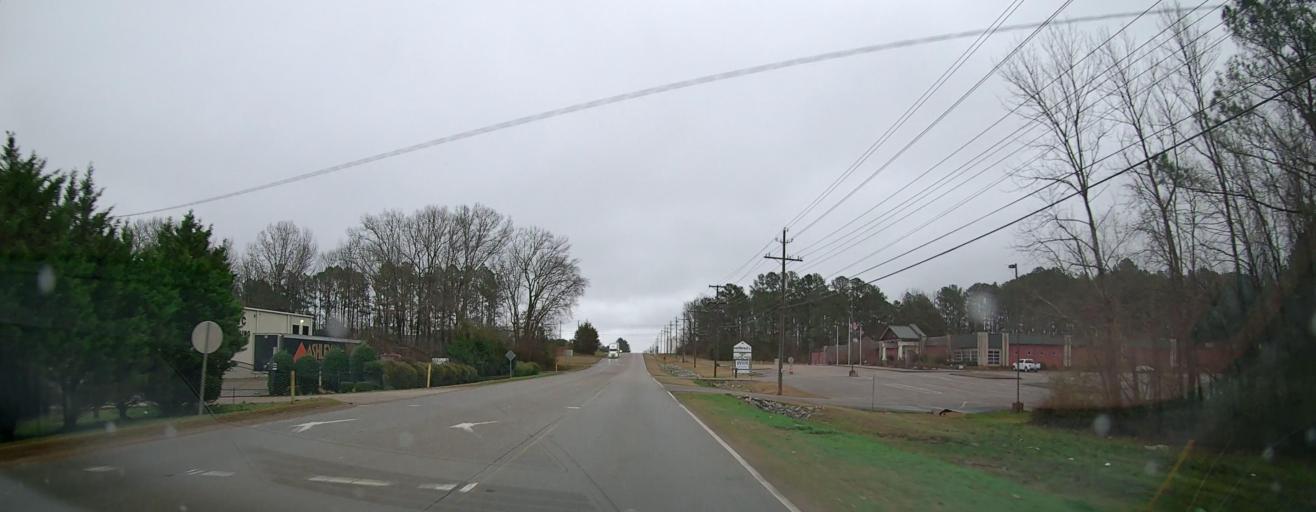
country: US
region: Mississippi
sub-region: Alcorn County
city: Corinth
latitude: 34.9089
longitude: -88.5353
